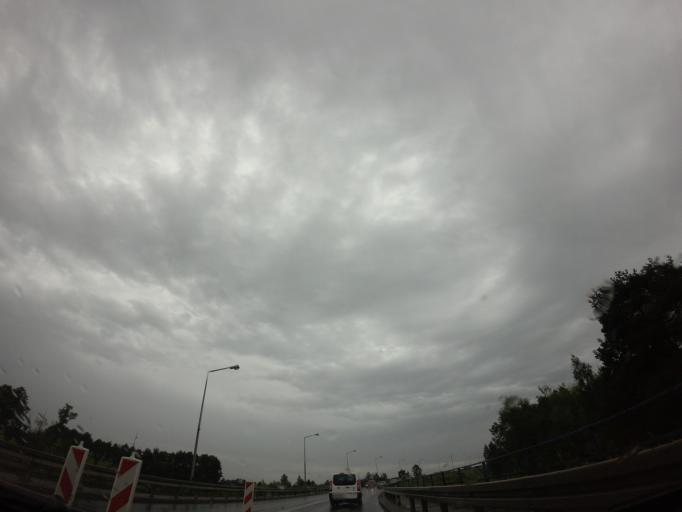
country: PL
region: Masovian Voivodeship
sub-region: Ostroleka
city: Ostroleka
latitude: 53.0884
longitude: 21.5607
